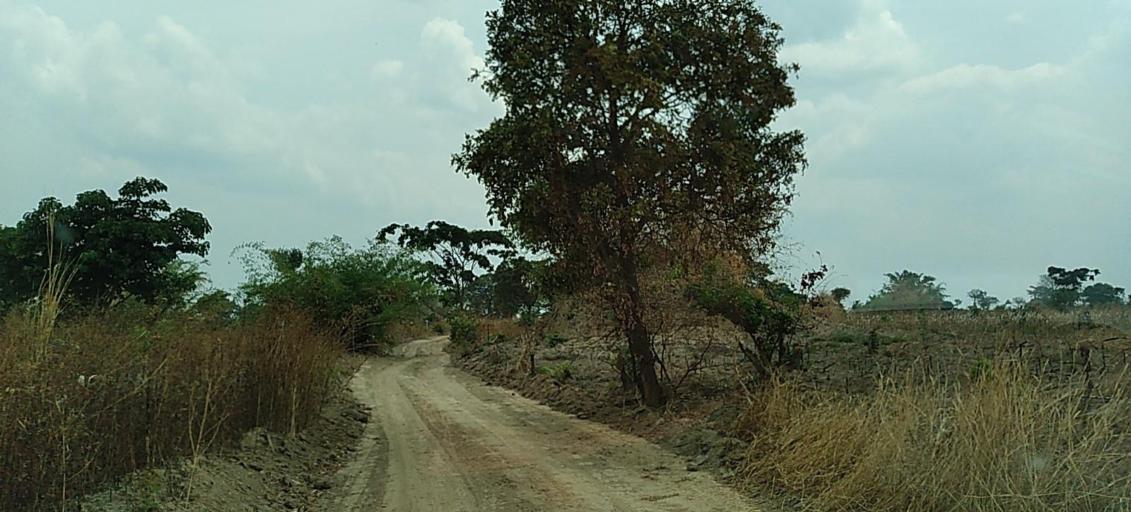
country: ZM
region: Copperbelt
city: Chililabombwe
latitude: -12.3527
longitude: 27.7973
